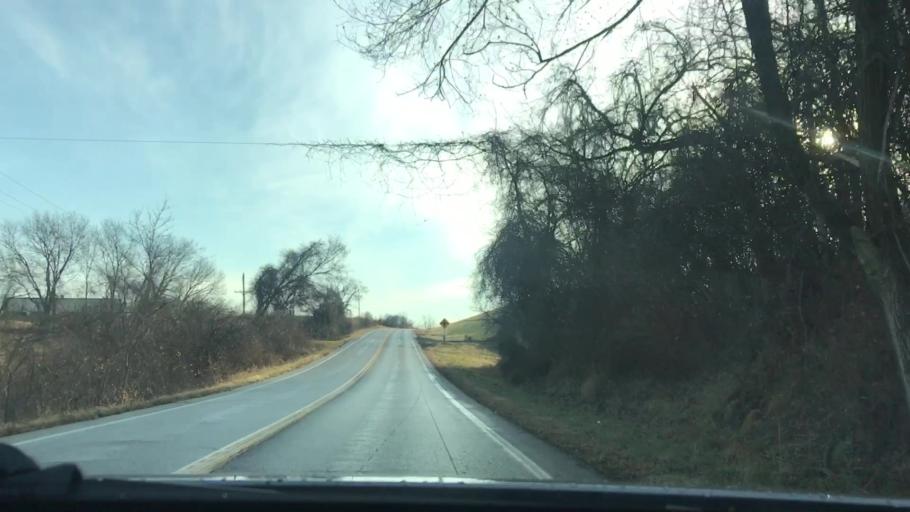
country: US
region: Missouri
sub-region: Platte County
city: Weatherby Lake
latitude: 39.2327
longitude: -94.7847
